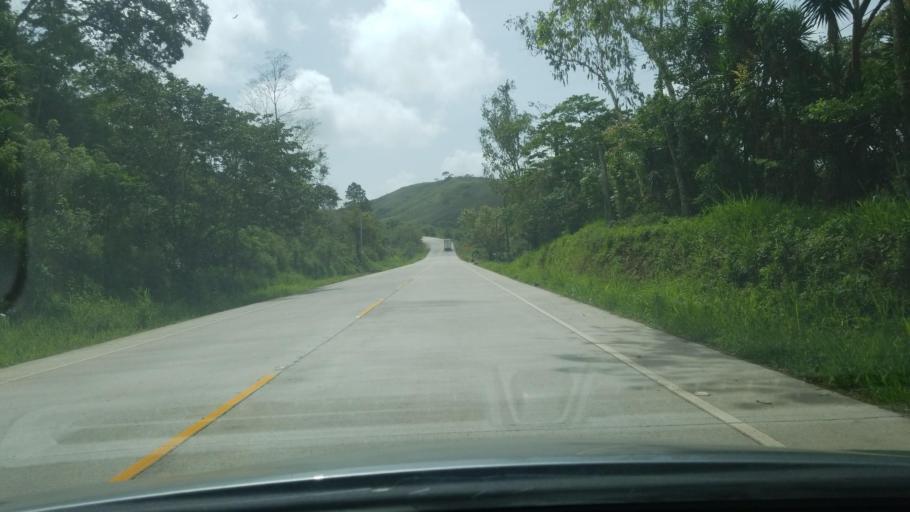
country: HN
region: Copan
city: San Jeronimo
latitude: 14.9346
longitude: -88.9263
